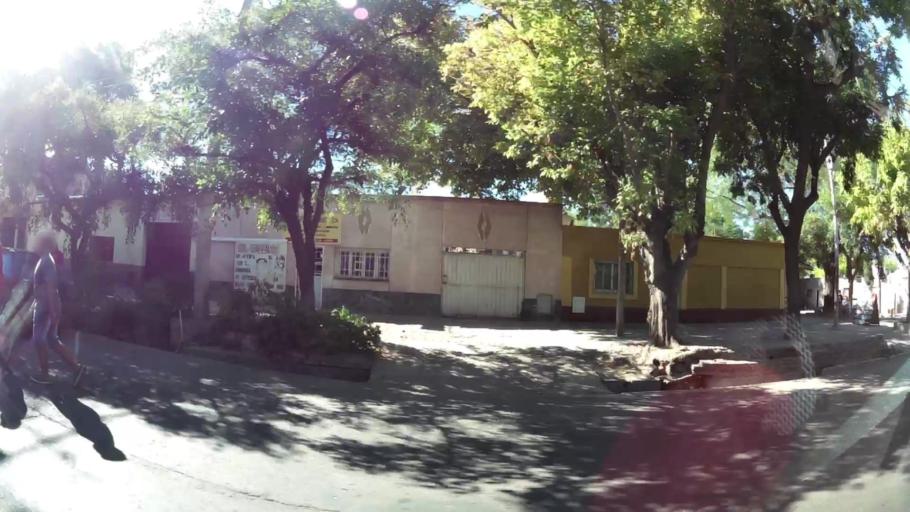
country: AR
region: Mendoza
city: Las Heras
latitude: -32.8420
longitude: -68.8227
